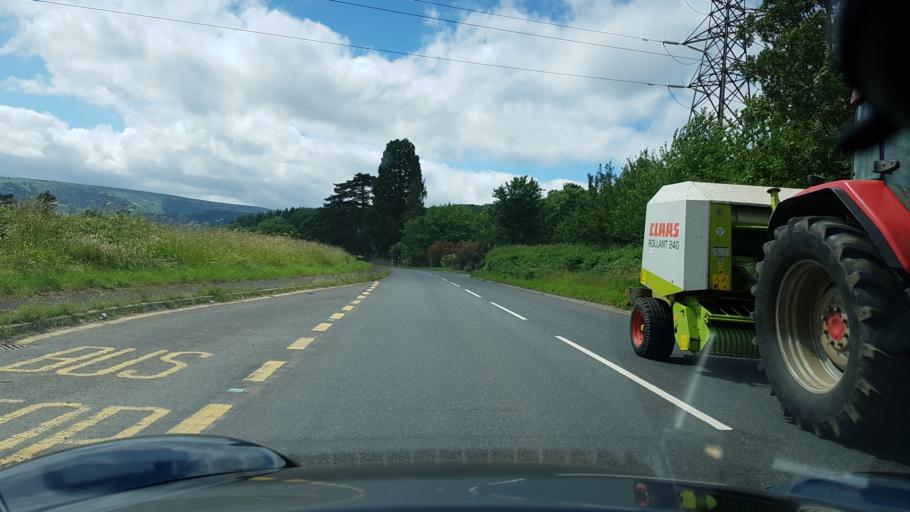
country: GB
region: Wales
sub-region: Monmouthshire
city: Abergavenny
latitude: 51.7865
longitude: -2.9665
